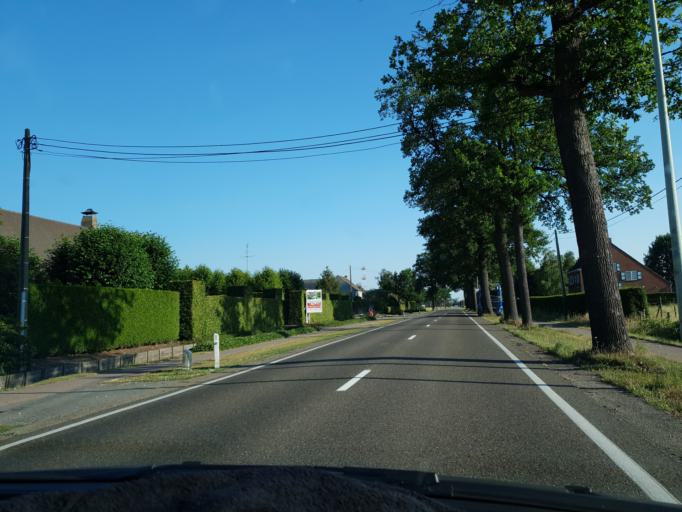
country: BE
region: Flanders
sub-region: Provincie Antwerpen
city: Hoogstraten
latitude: 51.3868
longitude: 4.7561
